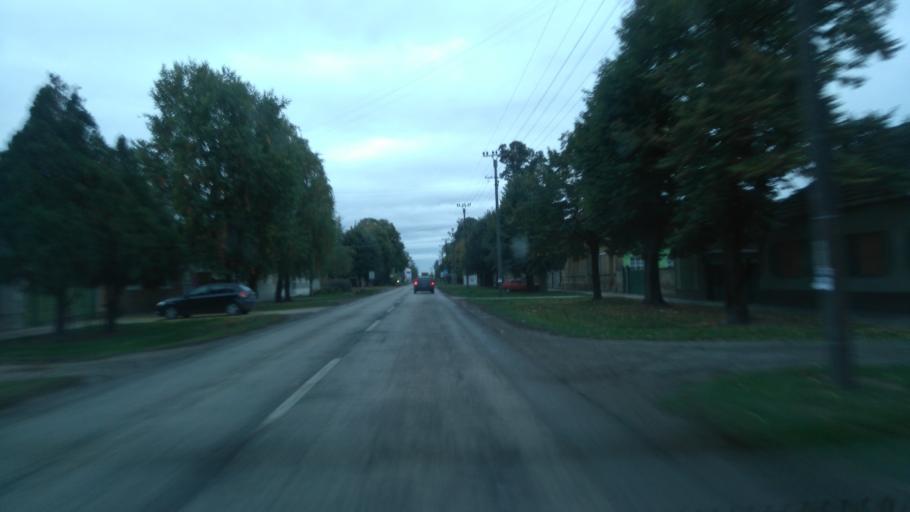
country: RS
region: Autonomna Pokrajina Vojvodina
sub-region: Juznobacki Okrug
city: Durdevo
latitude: 45.3194
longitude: 20.0671
